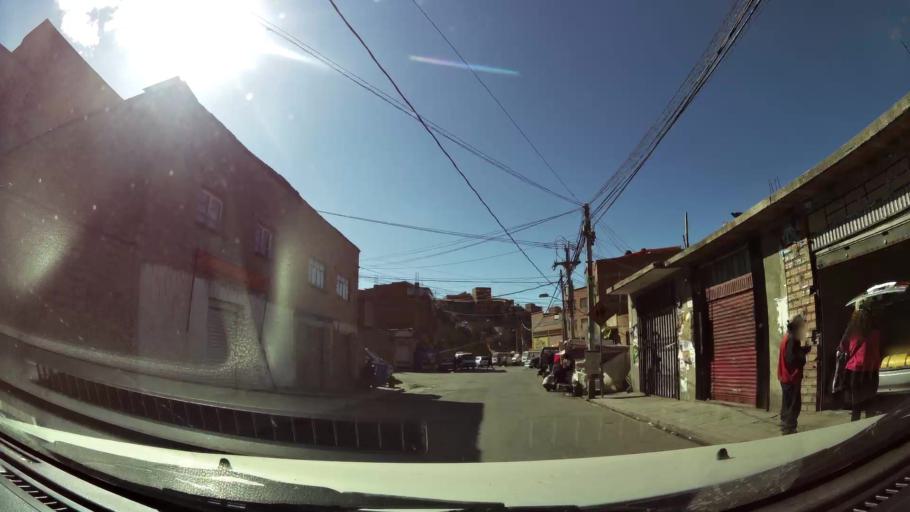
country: BO
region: La Paz
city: La Paz
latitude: -16.5121
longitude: -68.1483
